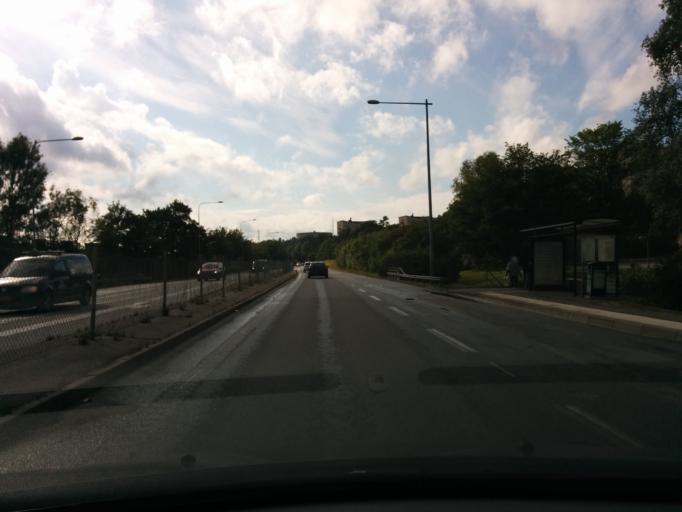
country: SE
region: Stockholm
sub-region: Sollentuna Kommun
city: Sollentuna
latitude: 59.4438
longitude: 17.9651
